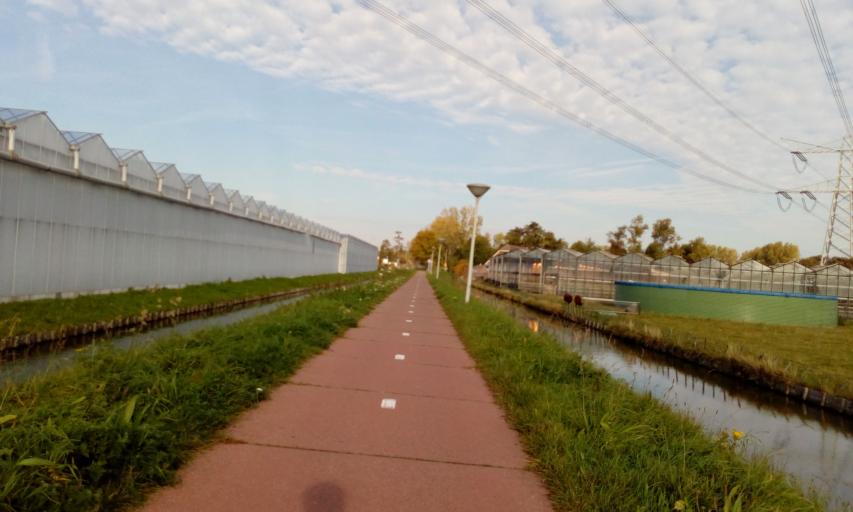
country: NL
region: South Holland
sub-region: Gemeente Westland
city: Naaldwijk
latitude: 51.9771
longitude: 4.2156
